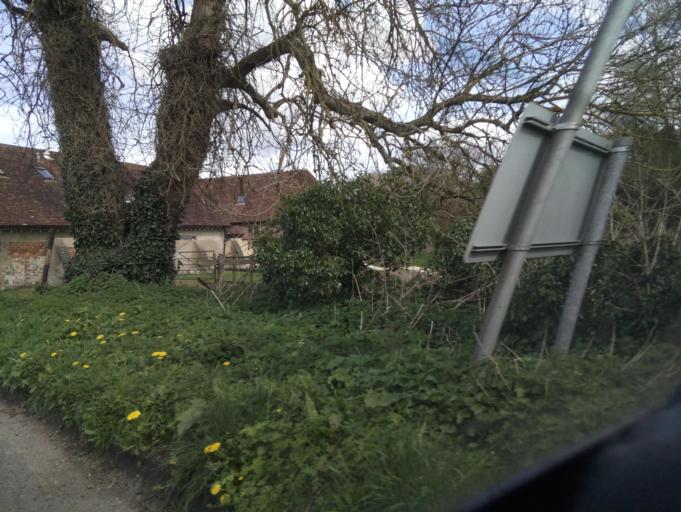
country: GB
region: England
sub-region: Hampshire
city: Abbotts Ann
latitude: 51.1062
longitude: -1.5039
